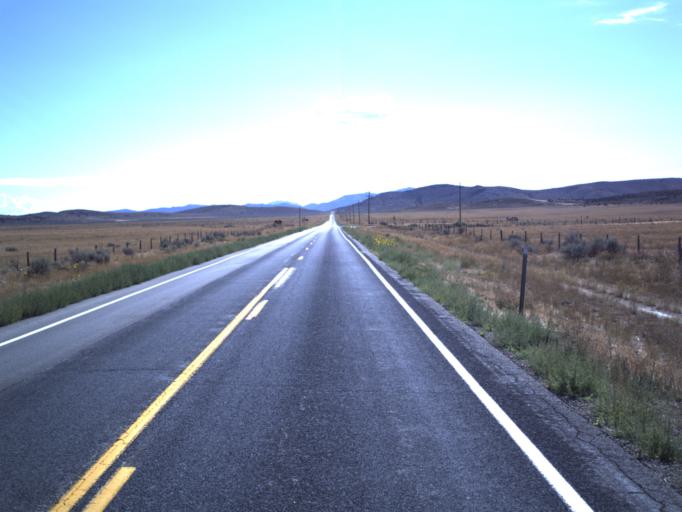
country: US
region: Utah
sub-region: Tooele County
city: Tooele
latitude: 40.0861
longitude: -112.4253
